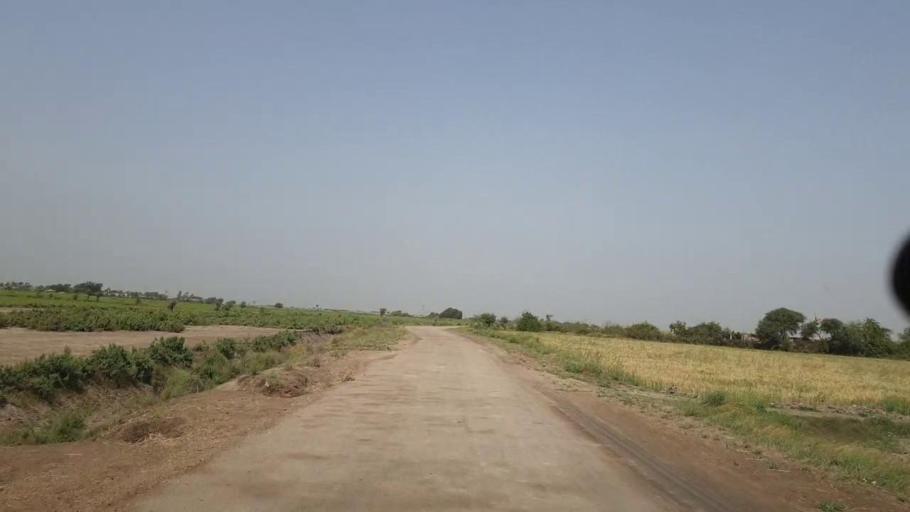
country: PK
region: Sindh
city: Matli
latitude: 25.0692
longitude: 68.6902
